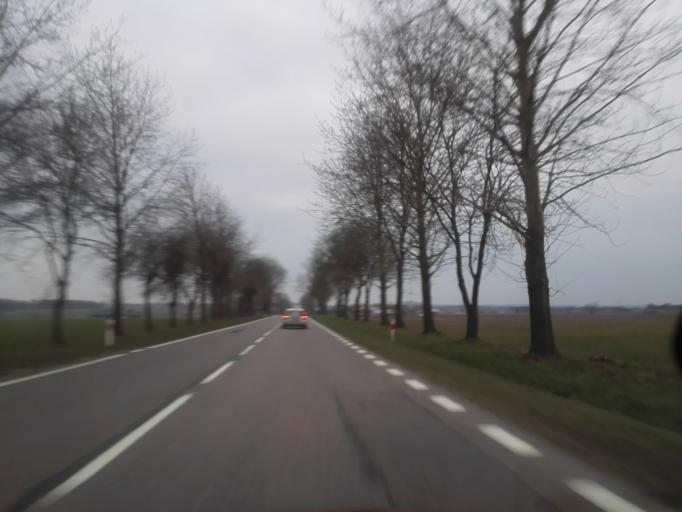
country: PL
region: Podlasie
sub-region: Powiat lomzynski
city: Piatnica
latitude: 53.2651
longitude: 22.1279
